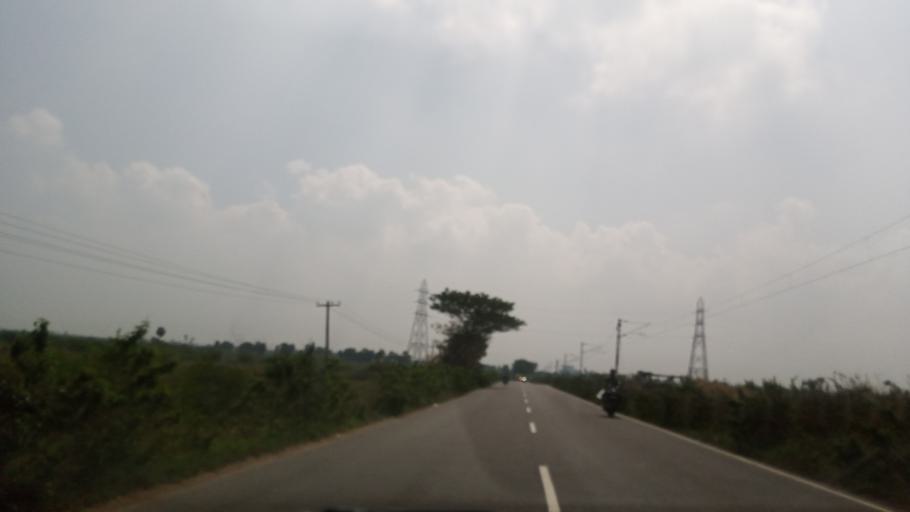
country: IN
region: Tamil Nadu
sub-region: Kancheepuram
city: Kanchipuram
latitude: 12.8892
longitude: 79.6870
